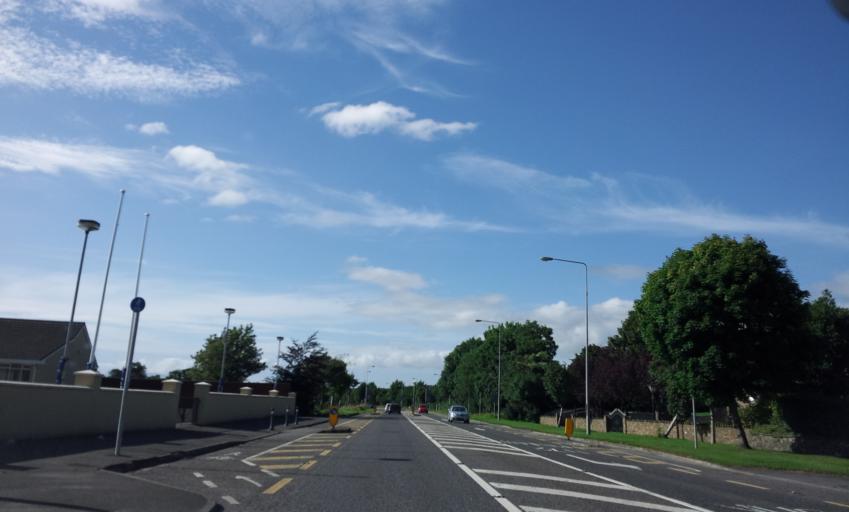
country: IE
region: Munster
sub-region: Ciarrai
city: Cill Airne
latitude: 52.0512
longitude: -9.4581
